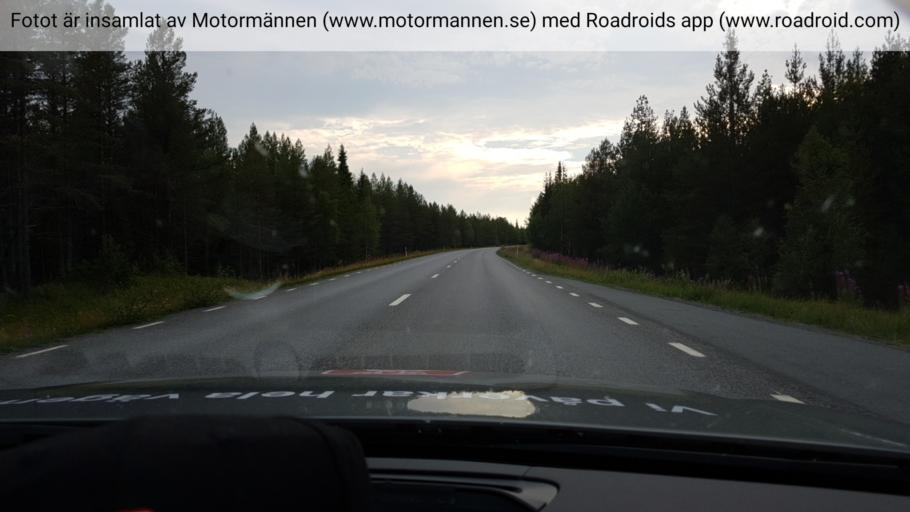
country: SE
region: Jaemtland
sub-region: OEstersunds Kommun
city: Lit
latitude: 63.3944
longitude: 15.0292
